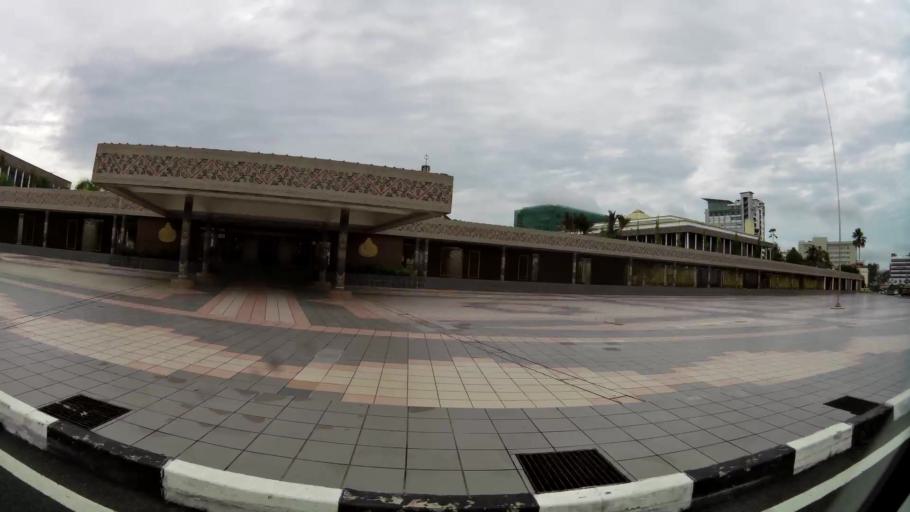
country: BN
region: Brunei and Muara
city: Bandar Seri Begawan
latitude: 4.8925
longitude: 114.9421
